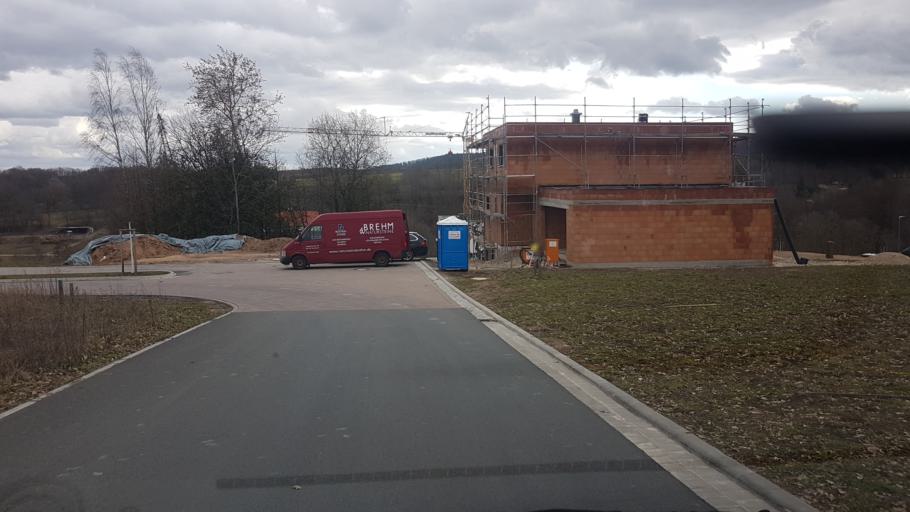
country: DE
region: Bavaria
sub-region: Upper Franconia
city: Baunach
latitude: 49.9841
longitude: 10.8376
